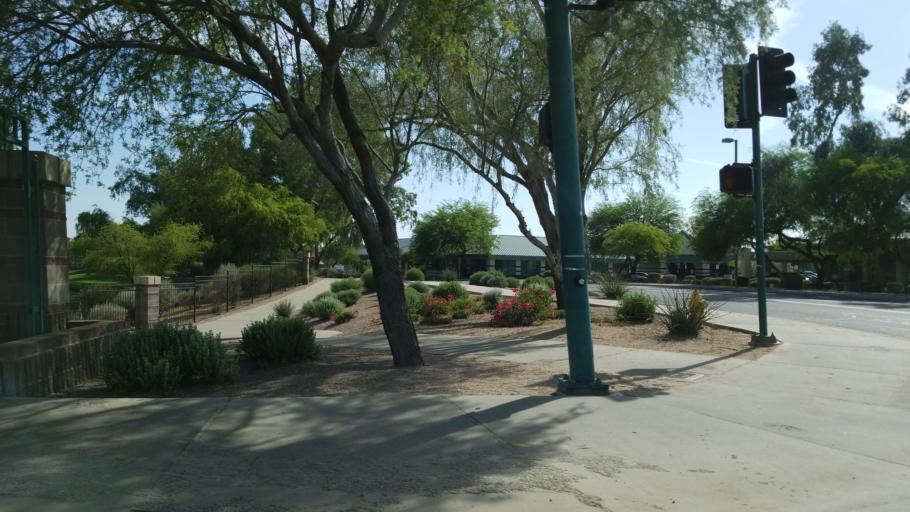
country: US
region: Arizona
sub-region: Maricopa County
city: Paradise Valley
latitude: 33.6248
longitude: -111.9393
